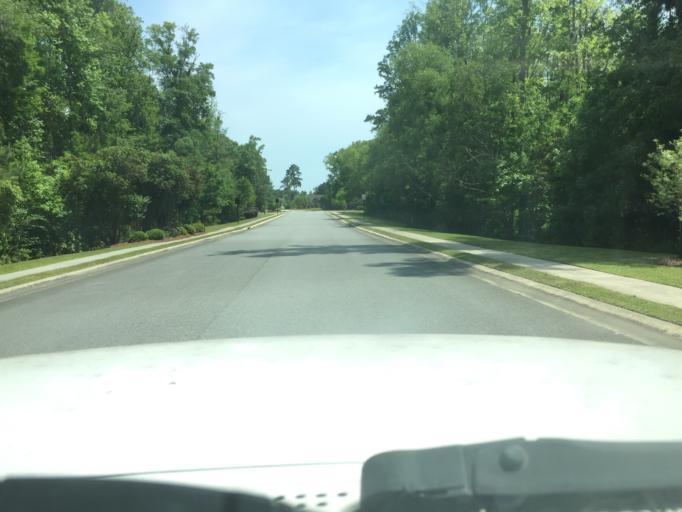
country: US
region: Georgia
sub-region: Chatham County
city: Pooler
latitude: 32.0611
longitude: -81.2429
